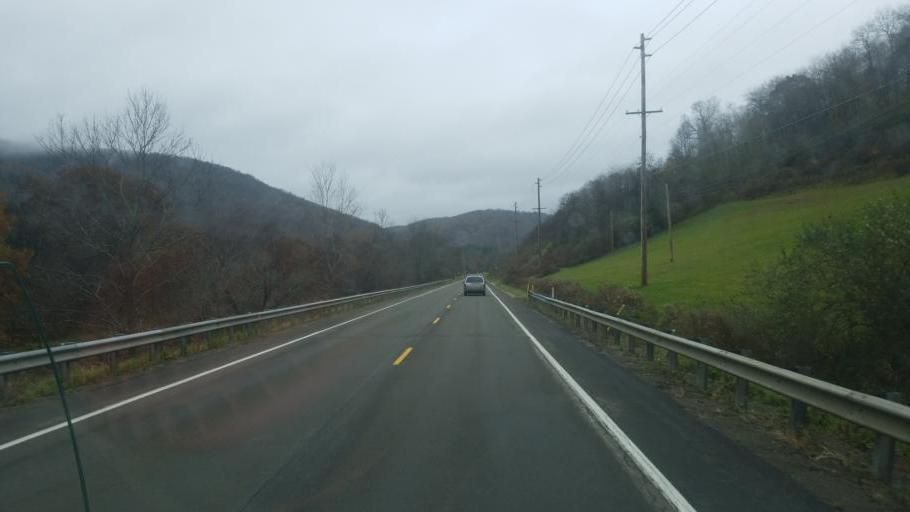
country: US
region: Pennsylvania
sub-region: Cameron County
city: Emporium
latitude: 41.4731
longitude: -78.3511
